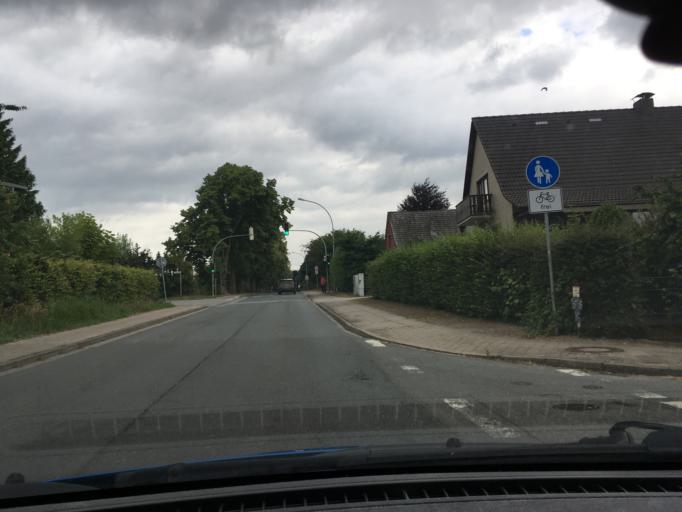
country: DE
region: Lower Saxony
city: Tostedt
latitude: 53.2771
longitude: 9.7362
